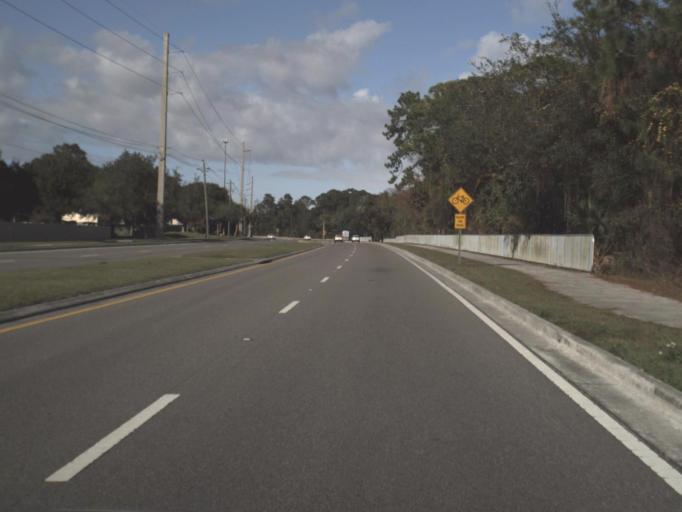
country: US
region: Florida
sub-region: Volusia County
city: Port Orange
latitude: 29.0981
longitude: -81.0288
